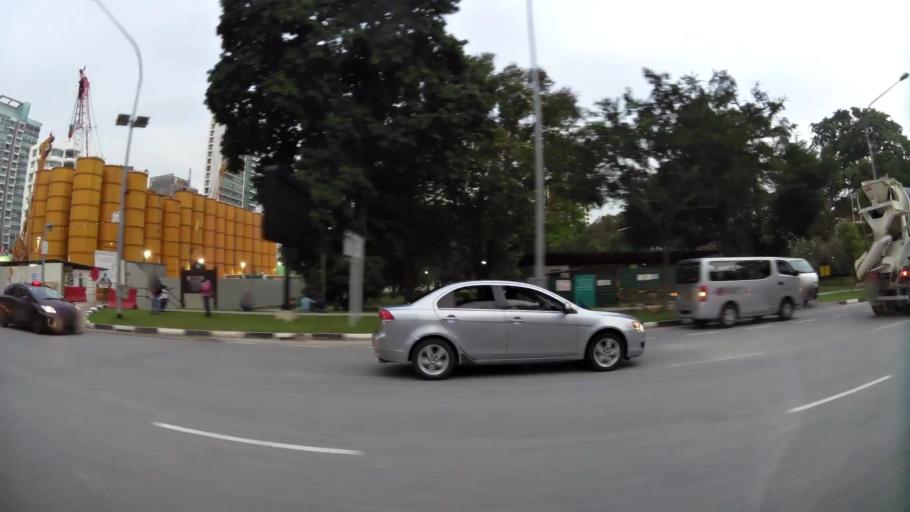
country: SG
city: Singapore
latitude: 1.2971
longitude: 103.8853
